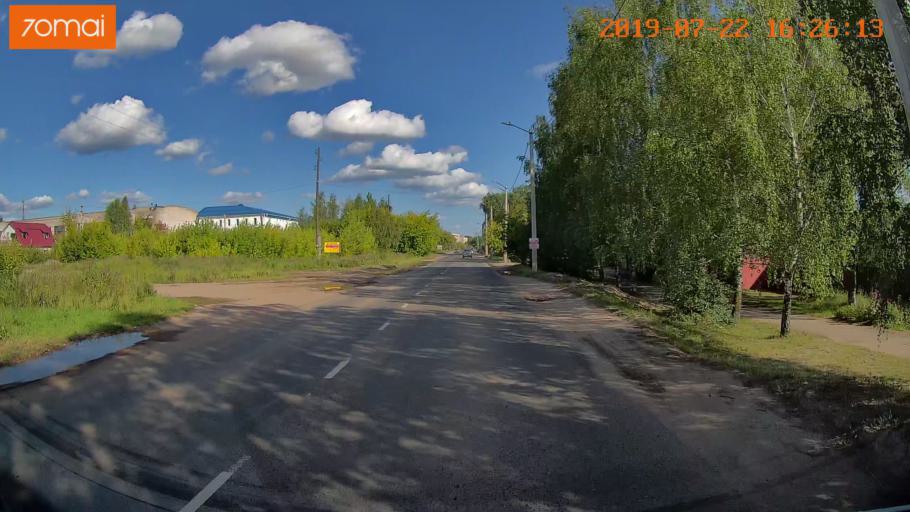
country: RU
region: Ivanovo
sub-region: Gorod Ivanovo
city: Ivanovo
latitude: 57.0501
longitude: 40.9316
